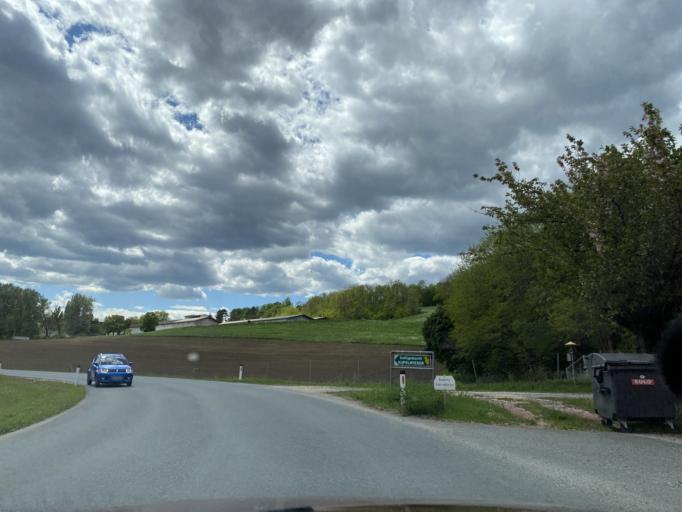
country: AT
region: Carinthia
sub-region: Politischer Bezirk Wolfsberg
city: Wolfsberg
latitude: 46.8465
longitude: 14.8383
